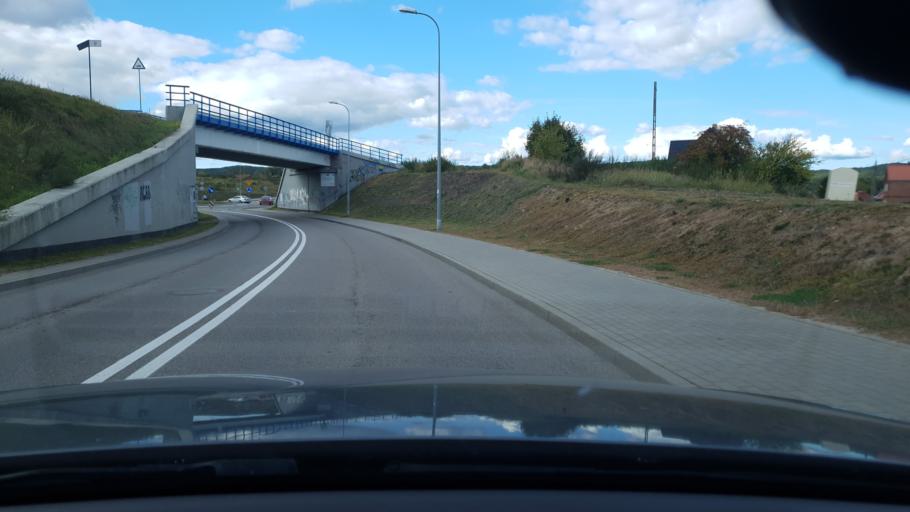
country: PL
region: Pomeranian Voivodeship
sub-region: Powiat wejherowski
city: Reda
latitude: 54.6011
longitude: 18.3467
